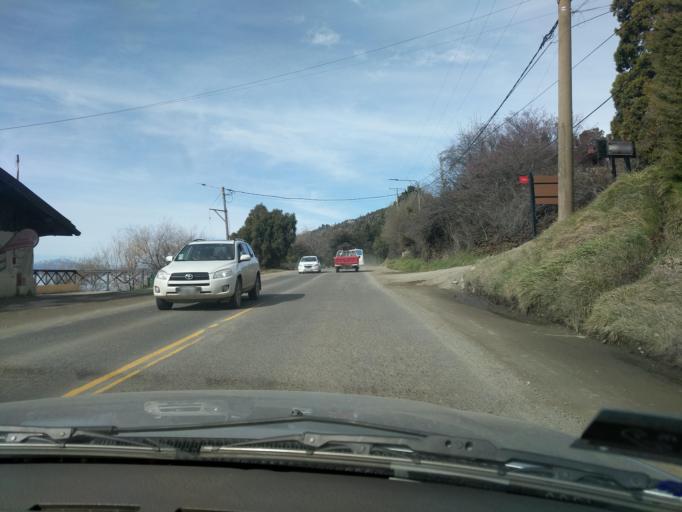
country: AR
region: Rio Negro
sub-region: Departamento de Bariloche
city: San Carlos de Bariloche
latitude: -41.1300
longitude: -71.3445
